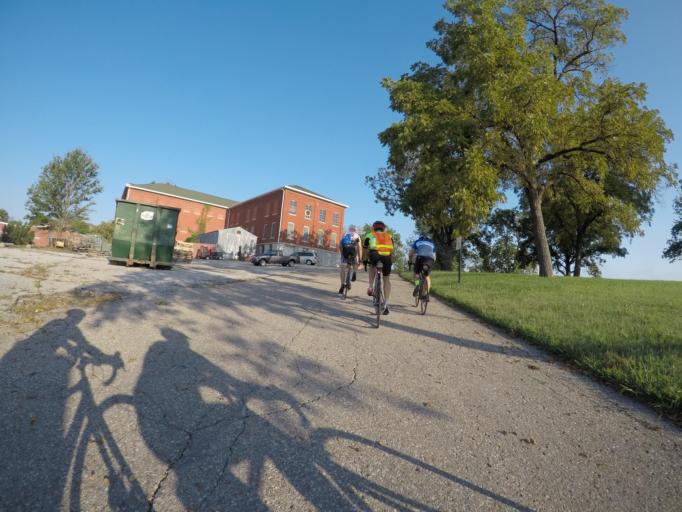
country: US
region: Kansas
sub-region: Leavenworth County
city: Lansing
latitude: 39.2802
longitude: -94.8929
